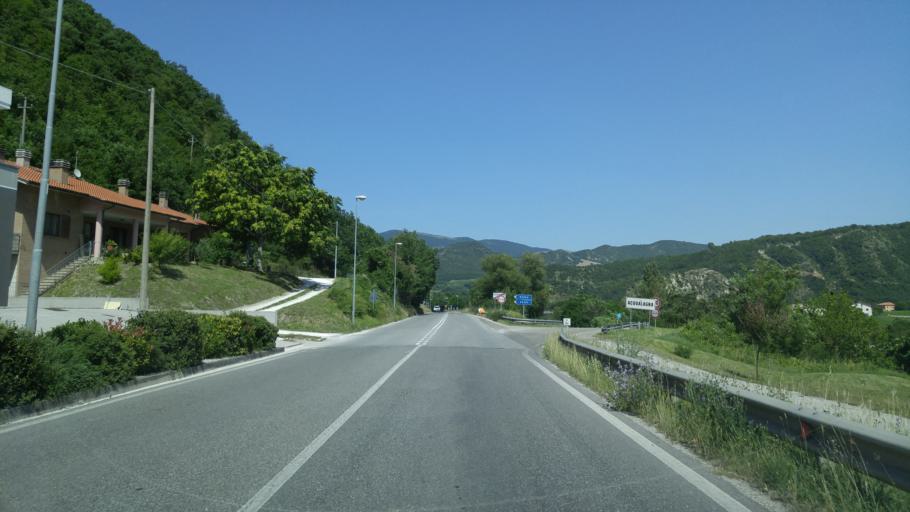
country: IT
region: The Marches
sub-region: Provincia di Pesaro e Urbino
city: Acqualagna
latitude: 43.6155
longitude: 12.6623
